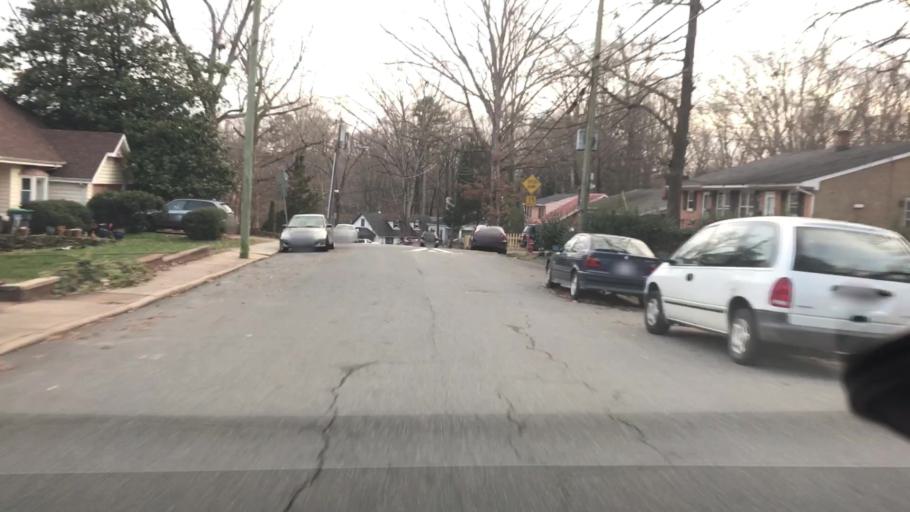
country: US
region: Virginia
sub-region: City of Charlottesville
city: Charlottesville
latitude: 38.0237
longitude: -78.5112
